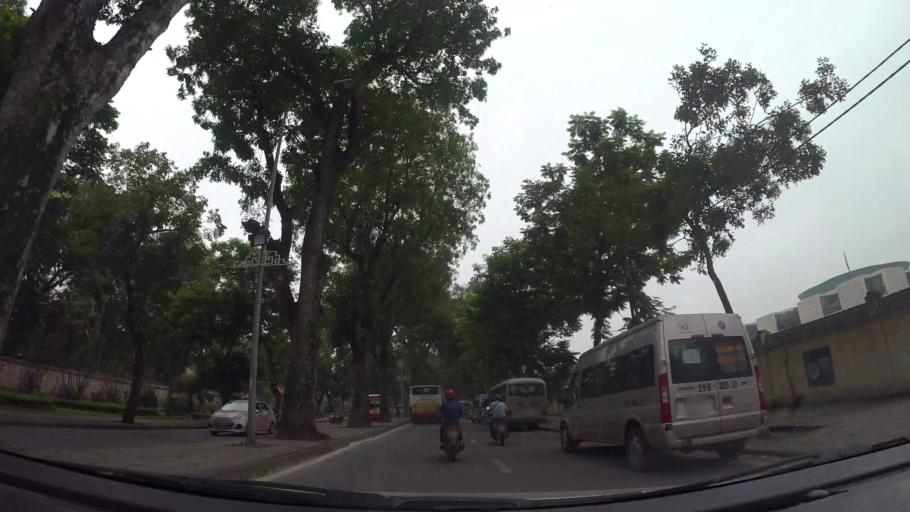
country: VN
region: Ha Noi
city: Hanoi
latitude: 21.0383
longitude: 105.8396
